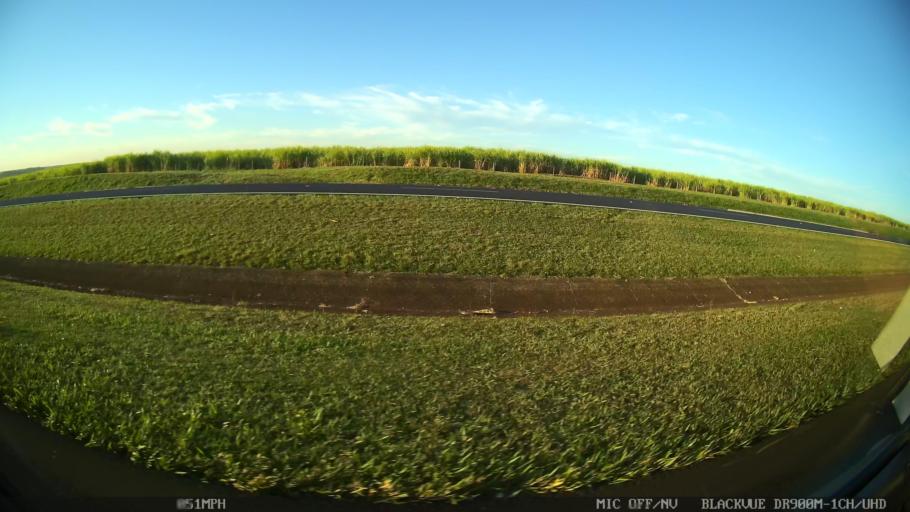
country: BR
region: Sao Paulo
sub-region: Ibate
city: Ibate
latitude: -21.8944
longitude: -48.0708
